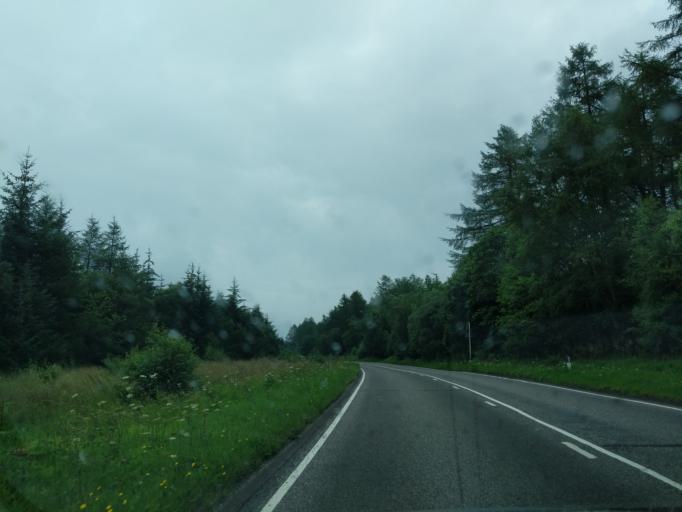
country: GB
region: Scotland
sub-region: Moray
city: Rothes
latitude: 57.4800
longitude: -3.1739
